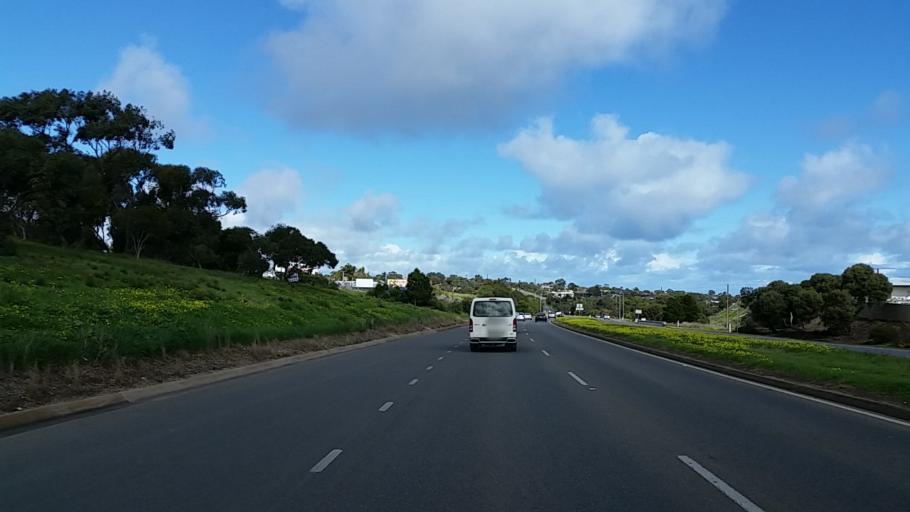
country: AU
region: South Australia
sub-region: Onkaparinga
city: Morphett Vale
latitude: -35.1181
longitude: 138.4903
